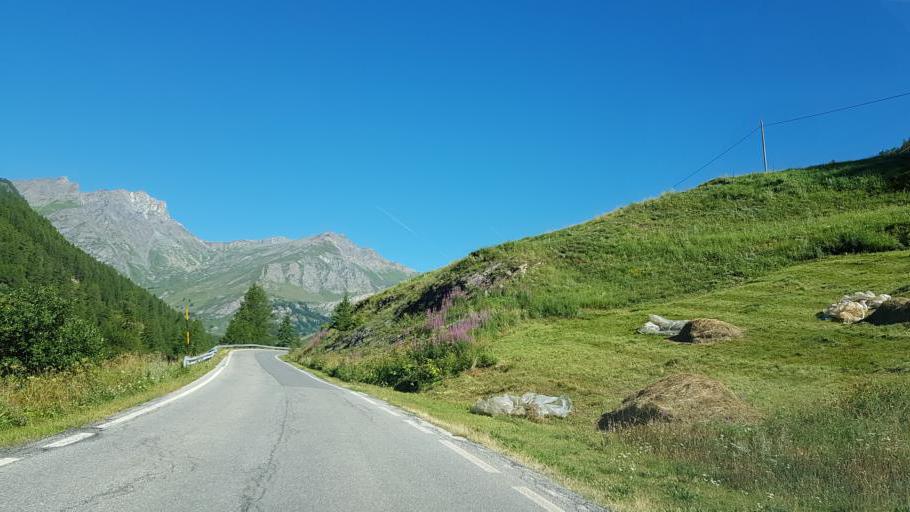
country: IT
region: Piedmont
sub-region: Provincia di Cuneo
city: Pontechianale
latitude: 44.6308
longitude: 7.0186
